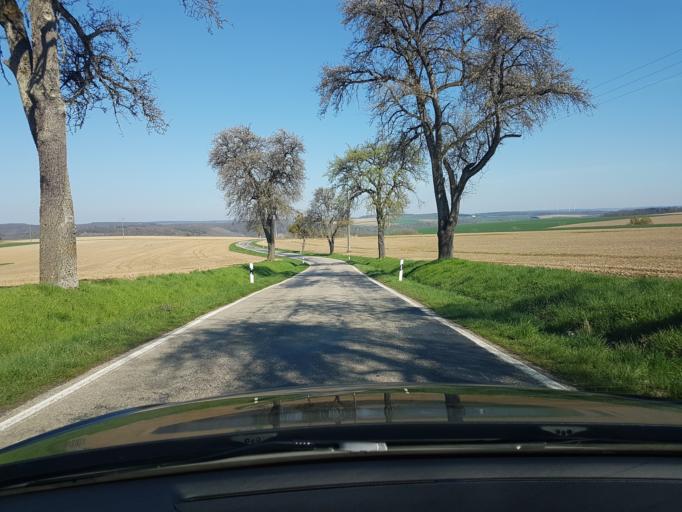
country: DE
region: Baden-Wuerttemberg
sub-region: Regierungsbezirk Stuttgart
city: Jagsthausen
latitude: 49.3177
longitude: 9.5141
